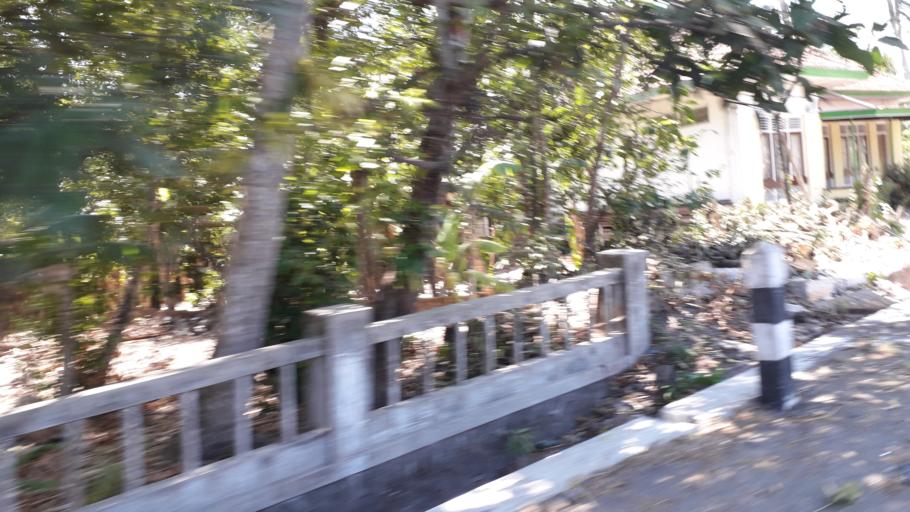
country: ID
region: Daerah Istimewa Yogyakarta
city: Pundong
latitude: -7.9842
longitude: 110.3161
